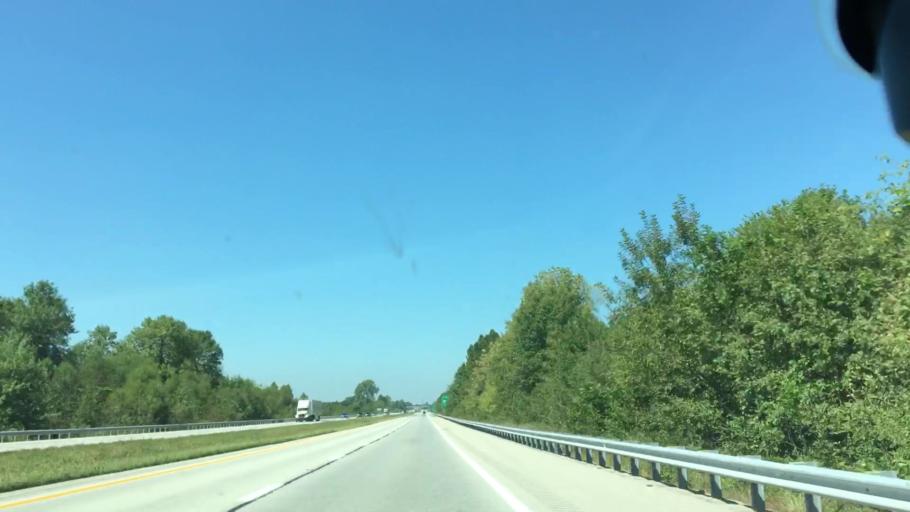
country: US
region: Kentucky
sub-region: Henderson County
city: Henderson
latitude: 37.7803
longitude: -87.5443
